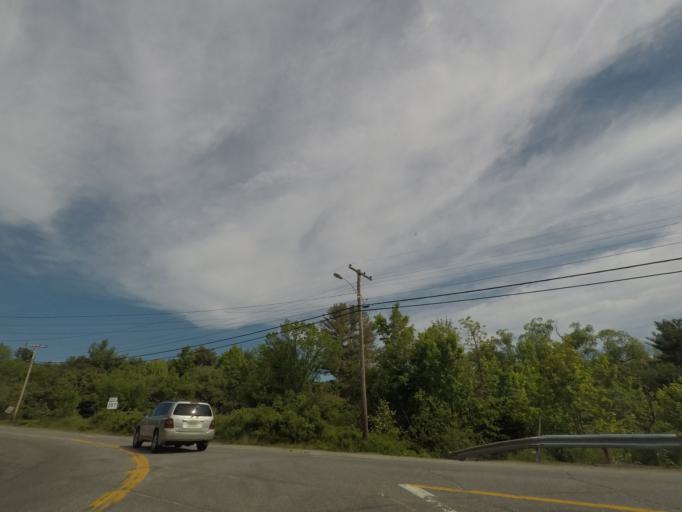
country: US
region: Maine
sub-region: Sagadahoc County
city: Richmond
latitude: 44.0919
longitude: -69.7921
